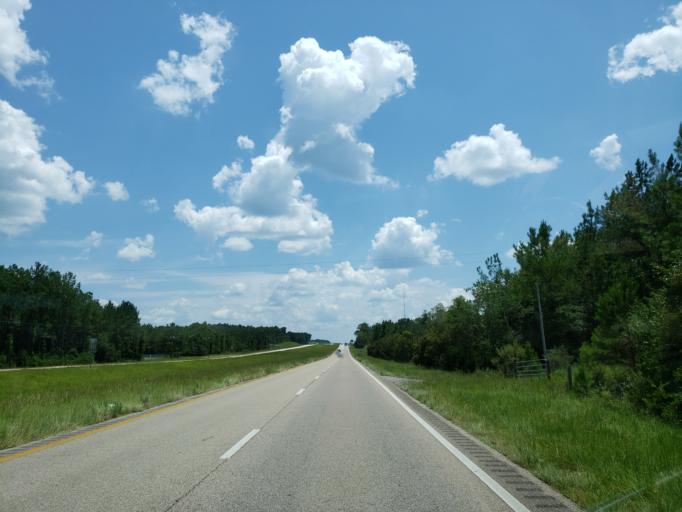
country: US
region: Mississippi
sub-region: Wayne County
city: Belmont
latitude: 31.4697
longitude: -88.4762
